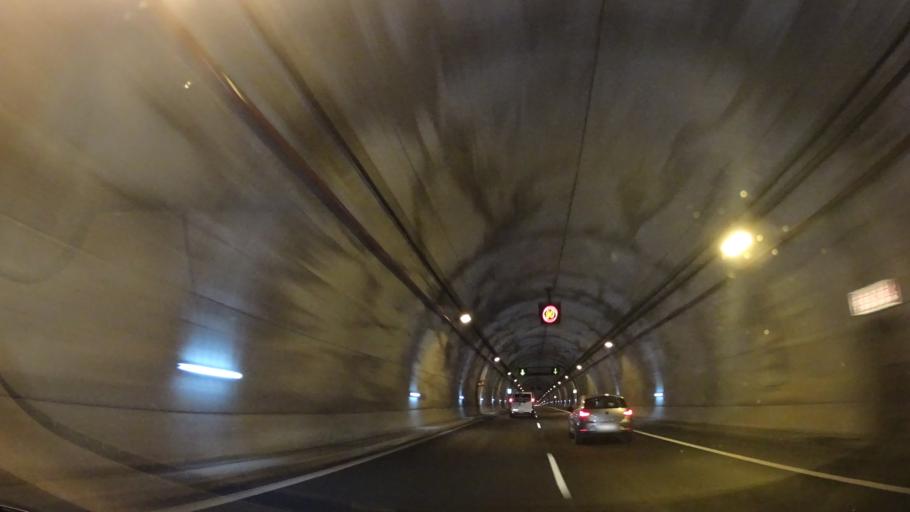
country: ES
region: Asturias
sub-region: Province of Asturias
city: Ribadesella
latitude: 43.4650
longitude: -5.1464
